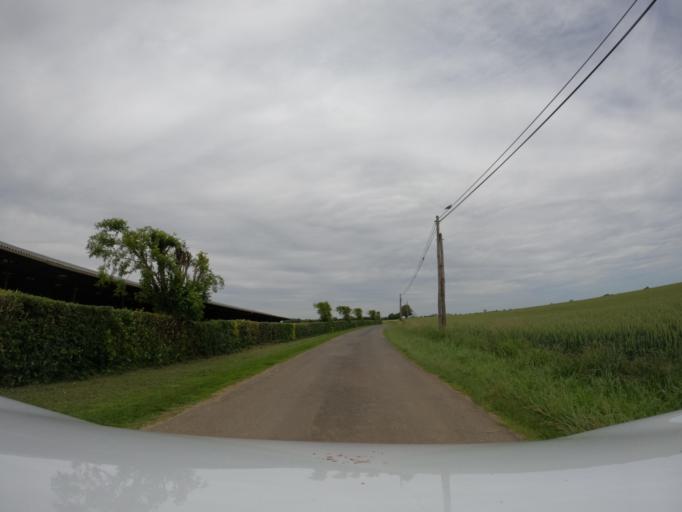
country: FR
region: Pays de la Loire
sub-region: Departement de la Vendee
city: Saint-Hilaire-des-Loges
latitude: 46.4818
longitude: -0.6454
